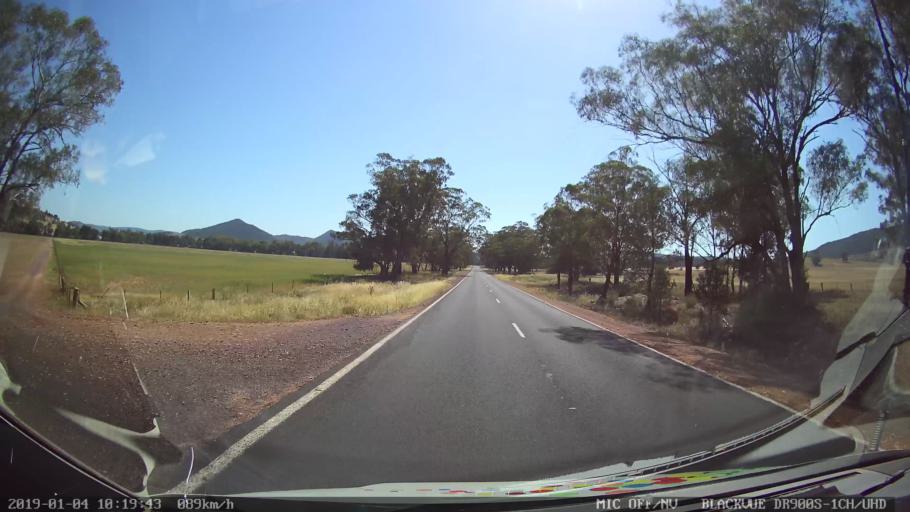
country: AU
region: New South Wales
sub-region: Cabonne
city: Canowindra
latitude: -33.3753
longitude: 148.4850
